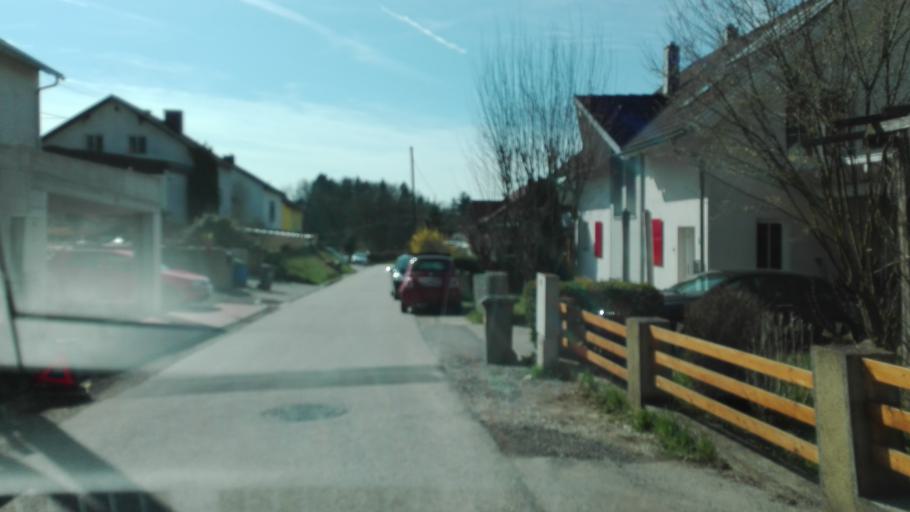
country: AT
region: Lower Austria
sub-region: Politischer Bezirk Amstetten
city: Ennsdorf
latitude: 48.2610
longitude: 14.5054
